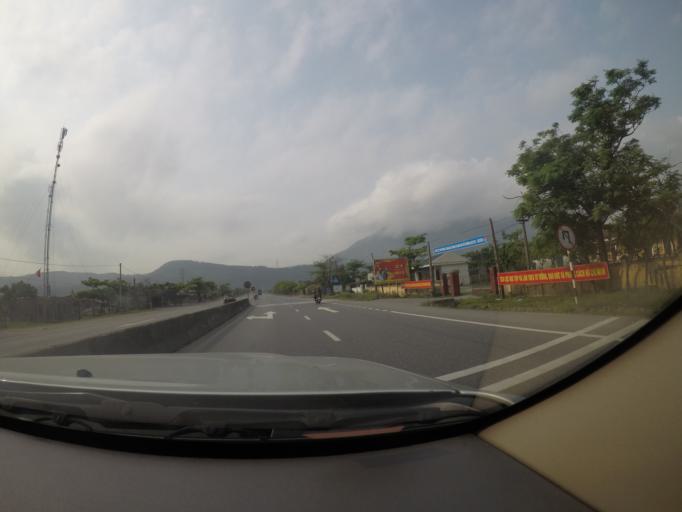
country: VN
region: Ha Tinh
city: Ky Anh
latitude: 17.9706
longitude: 106.4710
